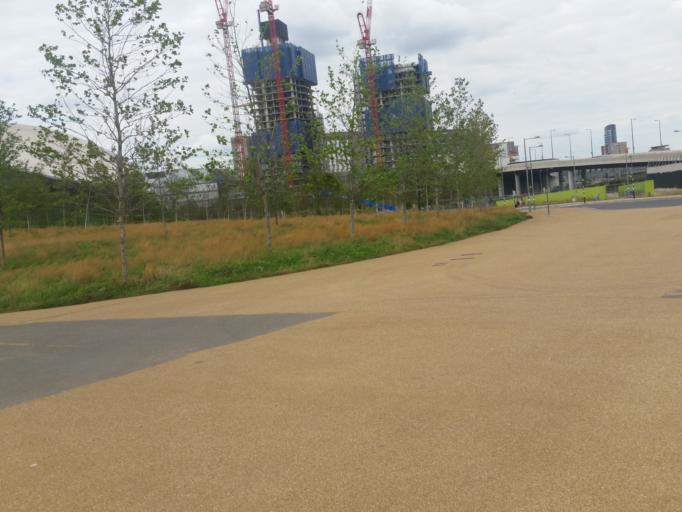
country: GB
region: England
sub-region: Greater London
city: Poplar
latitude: 51.5386
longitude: -0.0103
